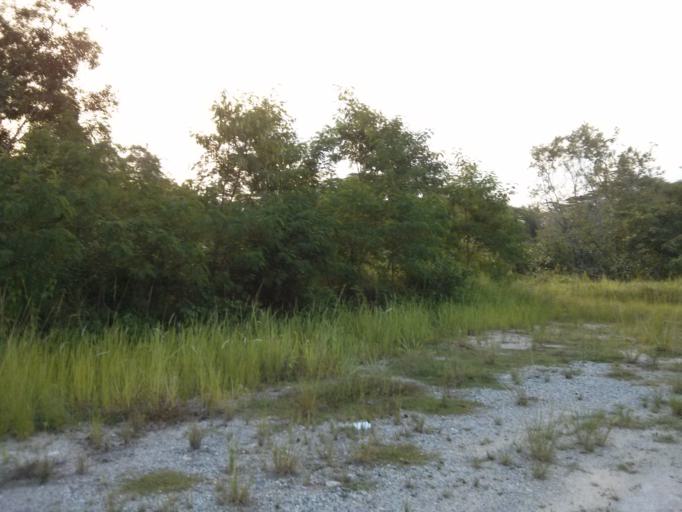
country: MY
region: Johor
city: Kampung Pasir Gudang Baru
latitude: 1.4330
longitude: 103.8617
